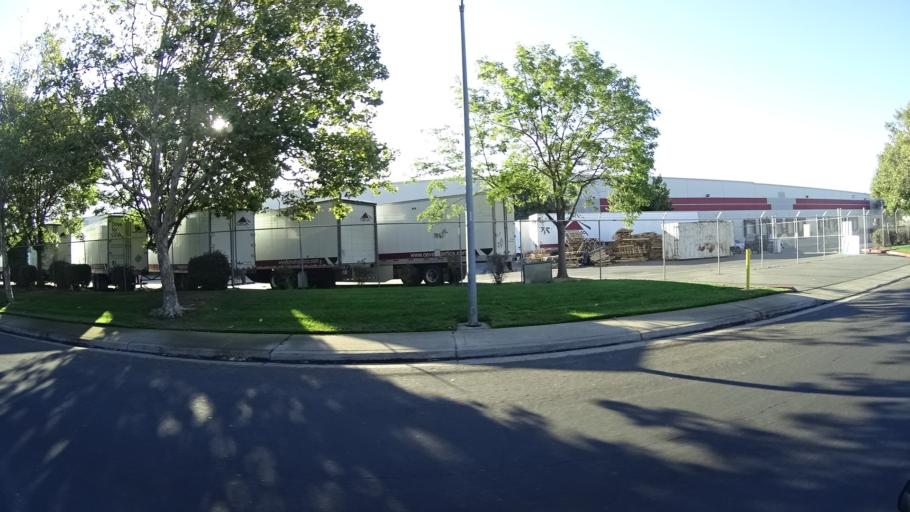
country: US
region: California
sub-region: Sacramento County
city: Florin
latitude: 38.5174
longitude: -121.3820
